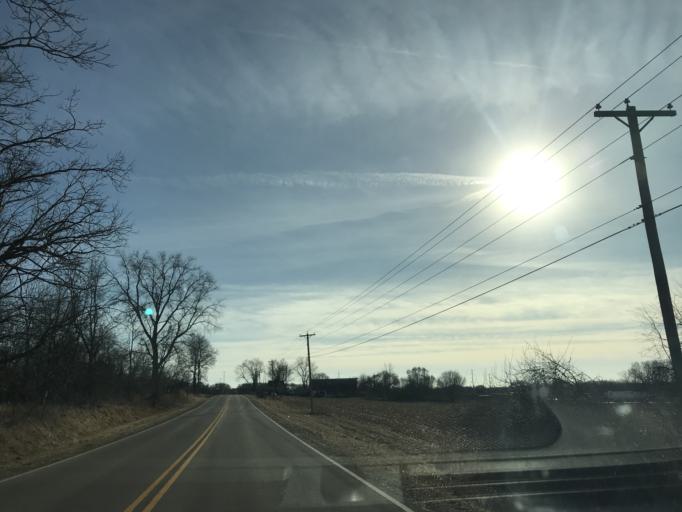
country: US
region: Wisconsin
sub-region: Dane County
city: Windsor
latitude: 43.1581
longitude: -89.3051
